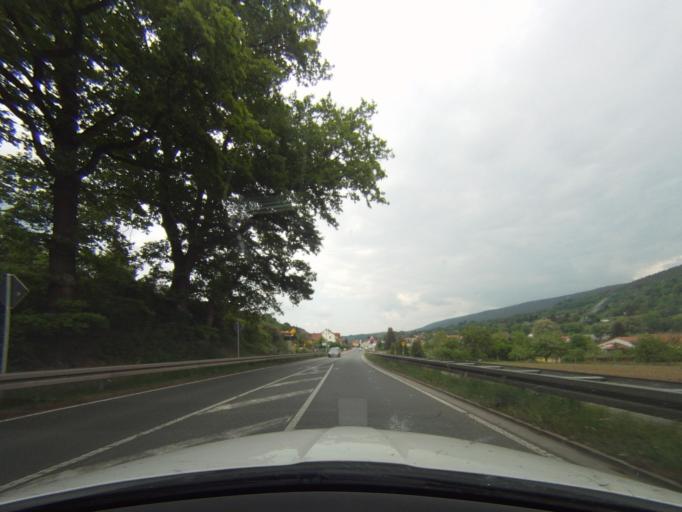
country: DE
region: Thuringia
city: Bad Blankenburg
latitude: 50.6873
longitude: 11.2504
